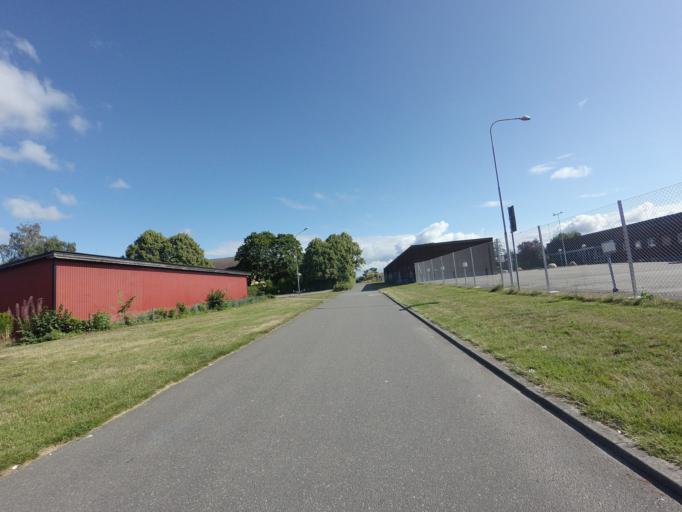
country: SE
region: Skane
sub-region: Hassleholms Kommun
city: Hassleholm
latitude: 56.1600
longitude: 13.7628
